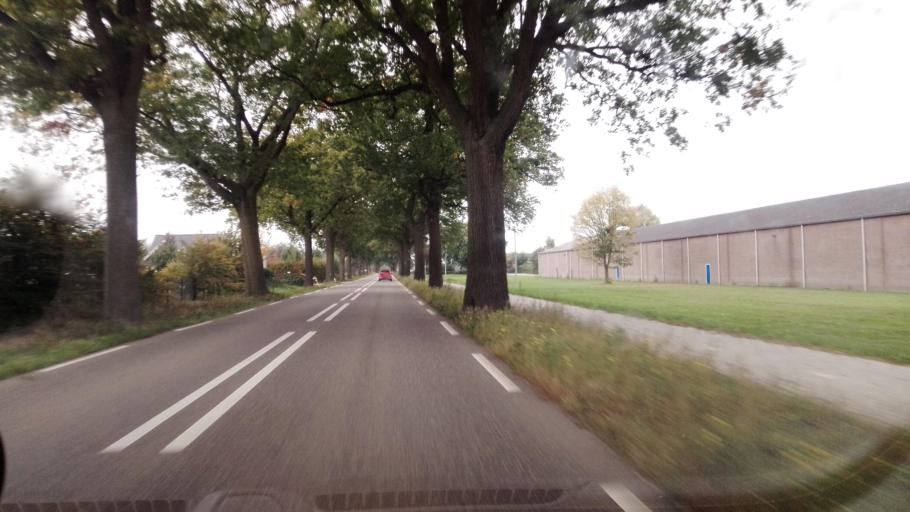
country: NL
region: Limburg
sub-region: Gemeente Peel en Maas
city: Maasbree
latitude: 51.4281
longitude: 6.0976
